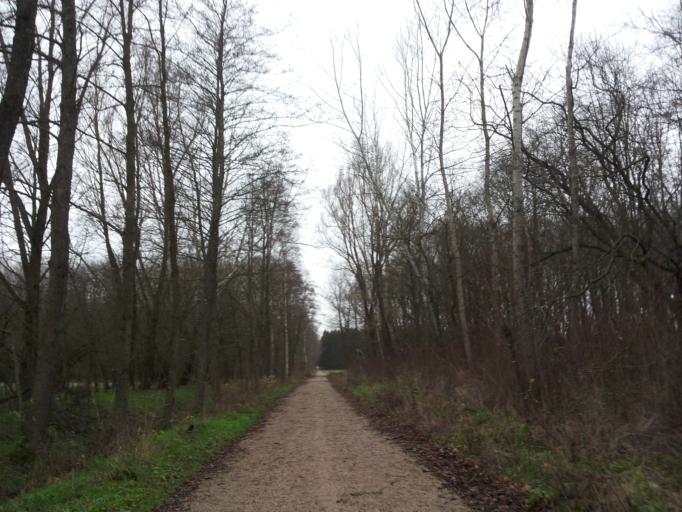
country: DE
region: Bavaria
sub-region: Regierungsbezirk Mittelfranken
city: Wendelstein
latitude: 49.3985
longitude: 11.1598
